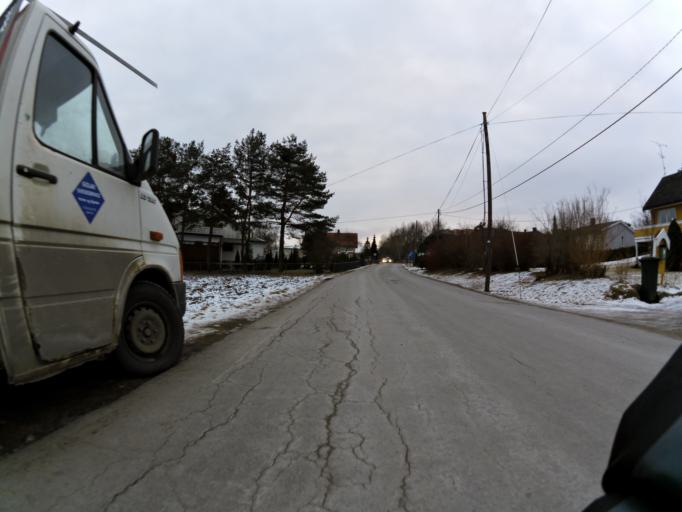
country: NO
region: Ostfold
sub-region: Fredrikstad
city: Fredrikstad
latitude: 59.2232
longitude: 10.8961
